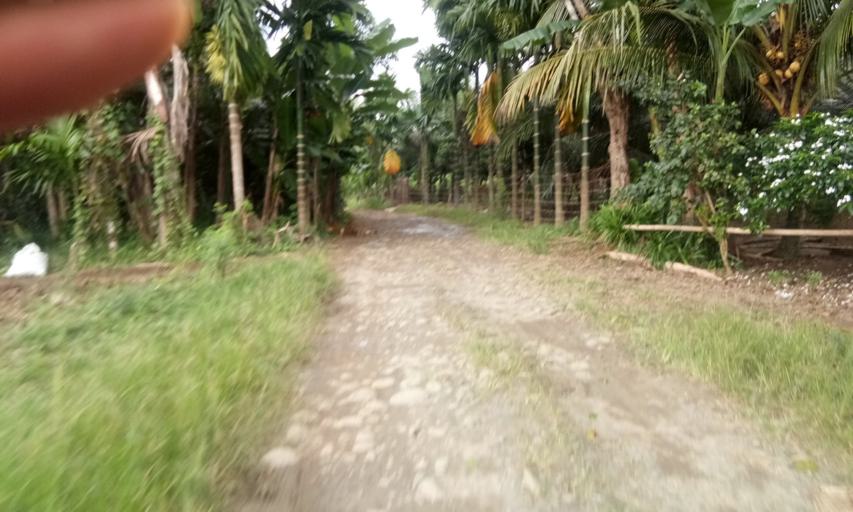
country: ID
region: North Sumatra
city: Deli Tua
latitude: 3.4691
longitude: 98.6108
